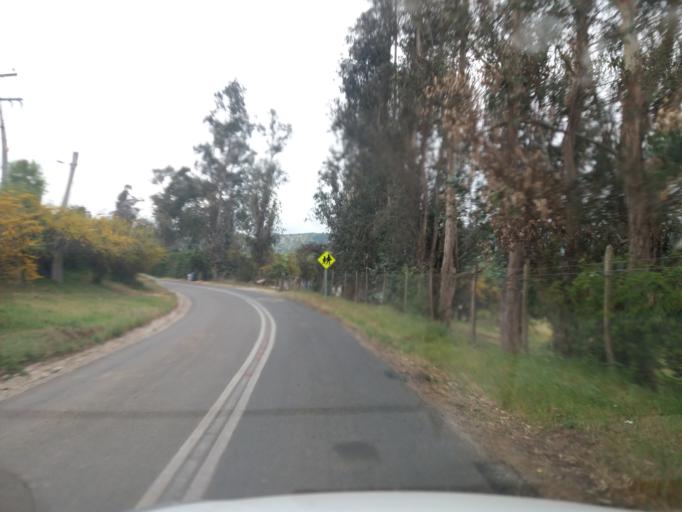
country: CL
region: Valparaiso
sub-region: Provincia de Quillota
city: Quillota
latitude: -32.8908
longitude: -71.3071
